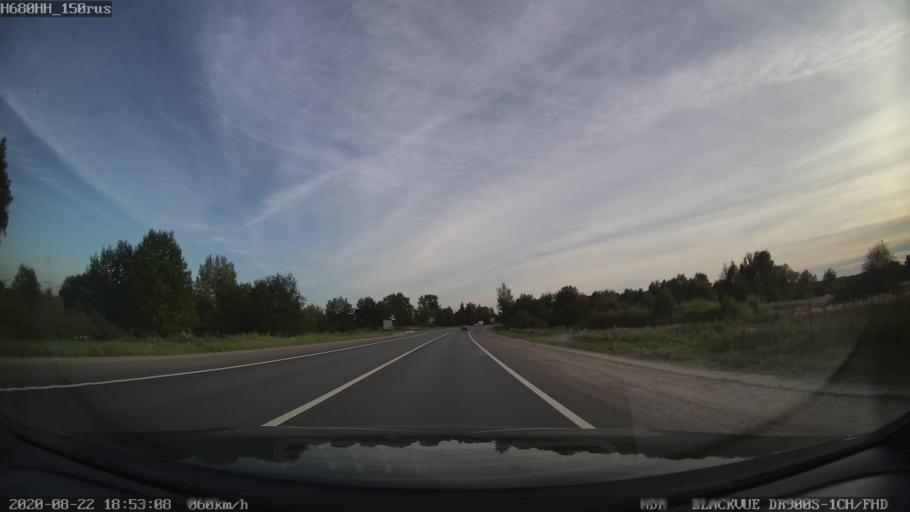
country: RU
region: Tverskaya
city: Rameshki
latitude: 57.2283
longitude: 36.0994
